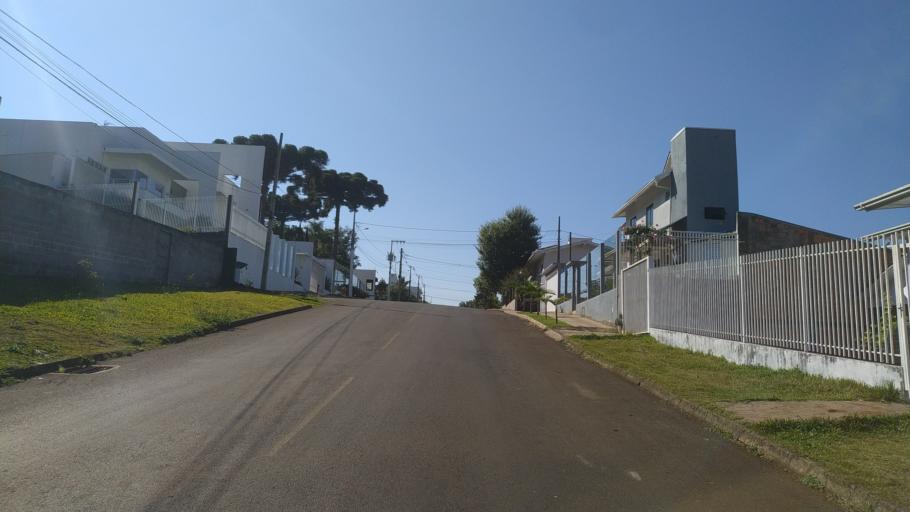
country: BR
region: Santa Catarina
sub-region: Chapeco
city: Chapeco
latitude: -27.0825
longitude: -52.6018
